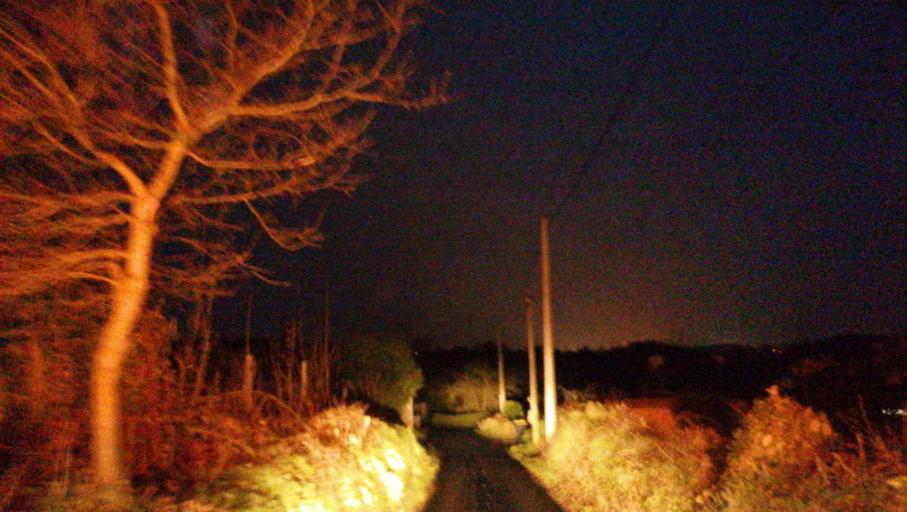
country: FR
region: Brittany
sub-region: Departement des Cotes-d'Armor
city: Plelo
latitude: 48.5572
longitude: -2.9763
